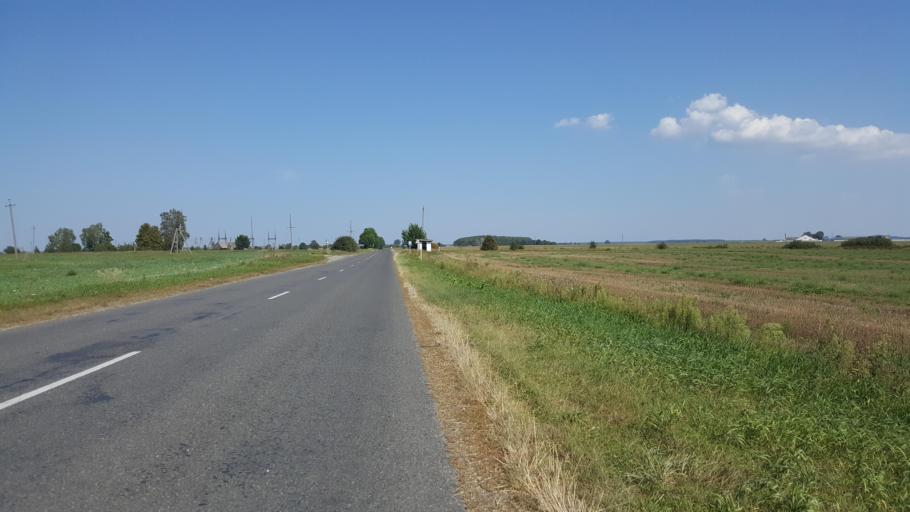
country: PL
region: Podlasie
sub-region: Powiat hajnowski
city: Czeremcha
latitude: 52.4813
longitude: 23.5349
